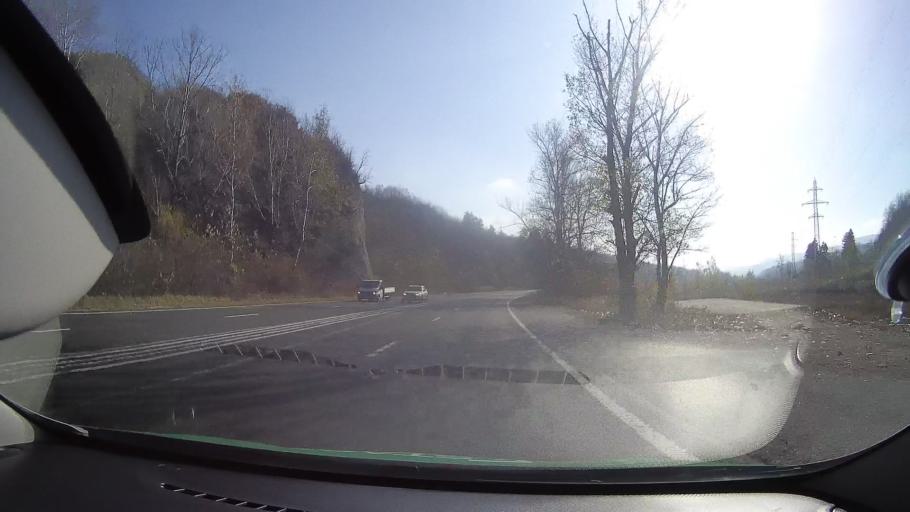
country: RO
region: Prahova
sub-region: Oras Breaza
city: Breaza de Jos
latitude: 45.1764
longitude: 25.6857
